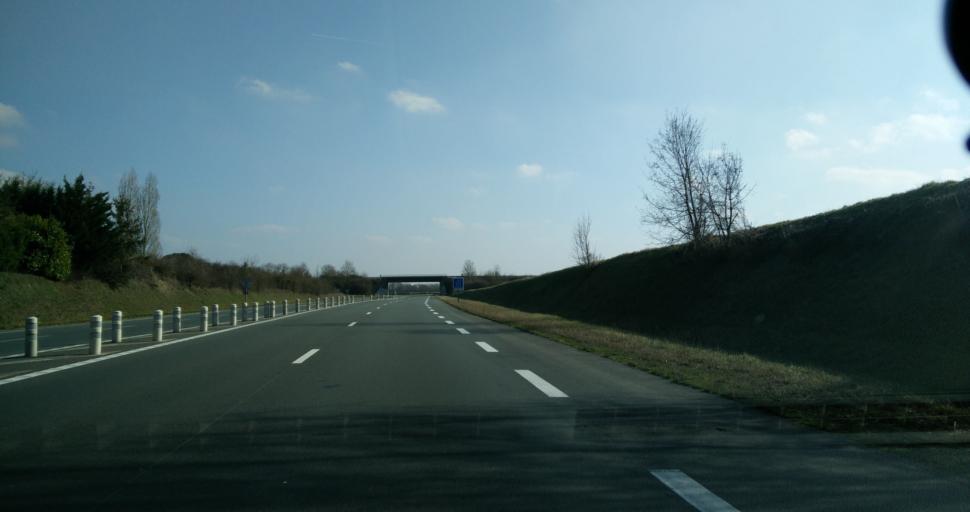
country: FR
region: Poitou-Charentes
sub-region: Departement des Deux-Sevres
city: Mauze-sur-le-Mignon
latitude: 46.1907
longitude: -0.6820
